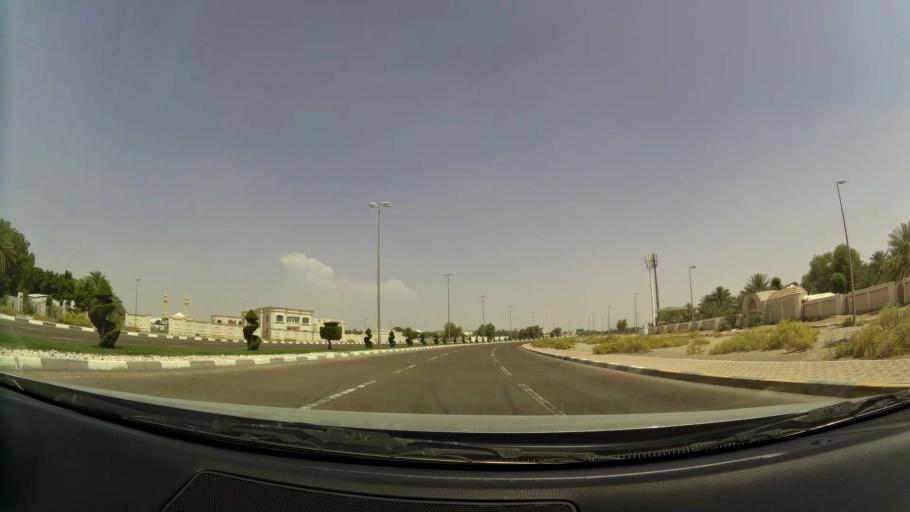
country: AE
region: Abu Dhabi
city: Al Ain
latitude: 24.2458
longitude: 55.6999
